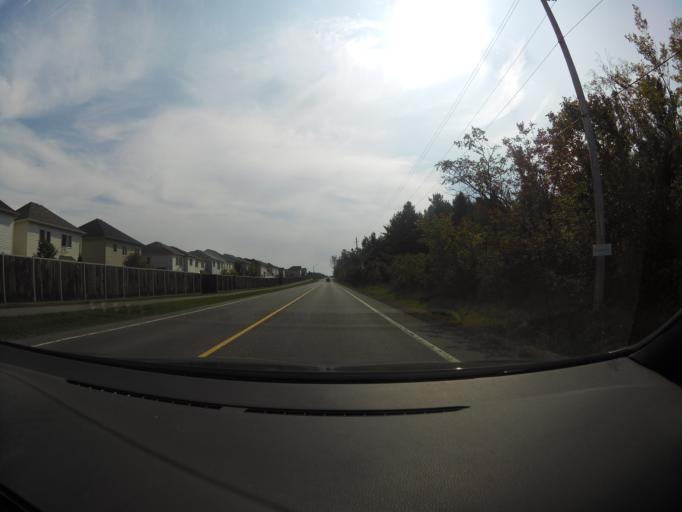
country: CA
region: Ontario
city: Bells Corners
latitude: 45.3480
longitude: -75.9486
